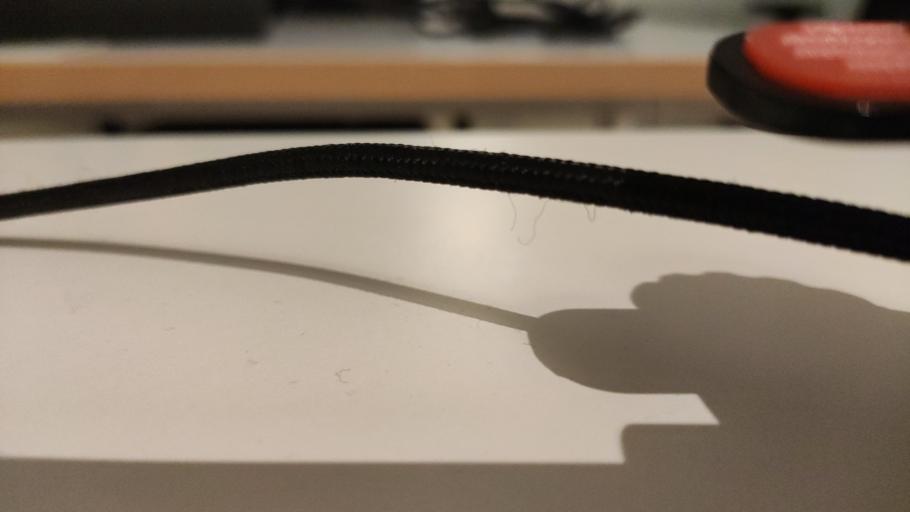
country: RU
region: Moskovskaya
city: Novosin'kovo
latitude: 56.3901
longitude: 37.3001
